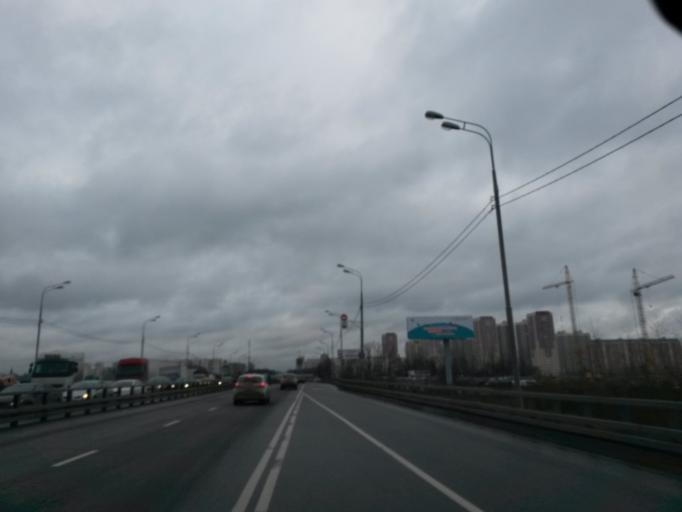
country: RU
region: Moskovskaya
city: Shcherbinka
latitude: 55.5231
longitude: 37.5785
